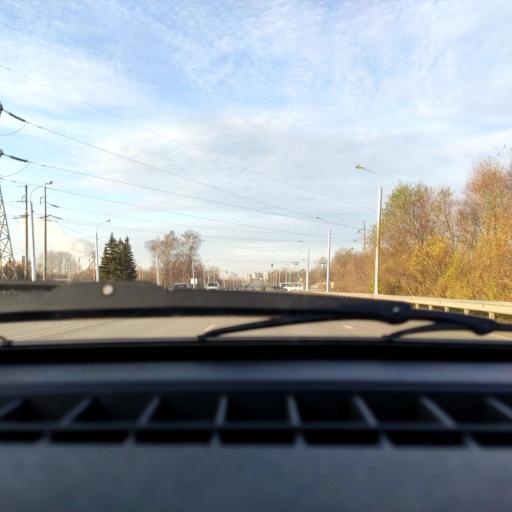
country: RU
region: Bashkortostan
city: Ufa
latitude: 54.8075
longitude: 56.1553
